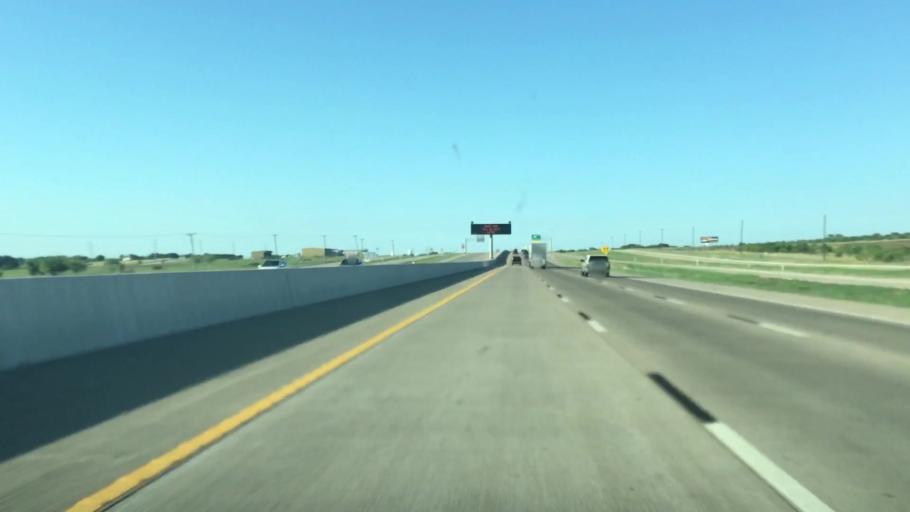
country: US
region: Texas
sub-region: McLennan County
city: Lorena
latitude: 31.4131
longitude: -97.1997
